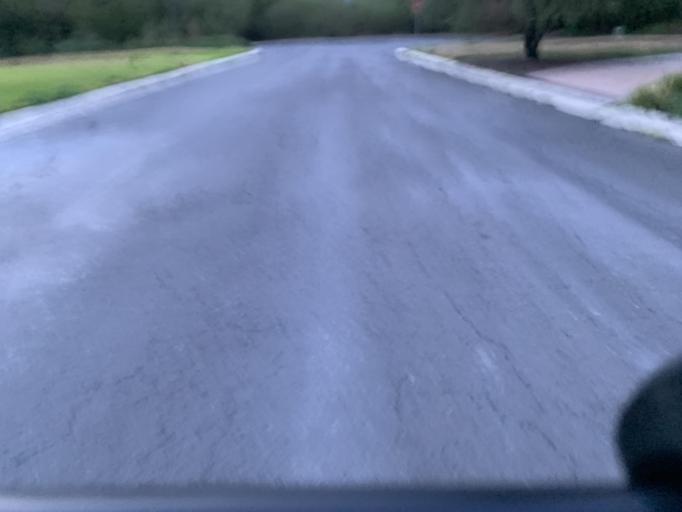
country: MX
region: Nuevo Leon
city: Santiago
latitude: 25.5093
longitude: -100.1882
